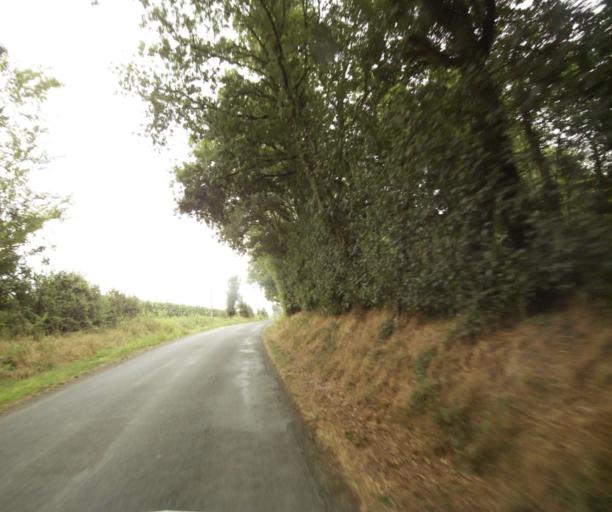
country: FR
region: Pays de la Loire
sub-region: Departement de la Sarthe
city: Juigne-sur-Sarthe
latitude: 47.8504
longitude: -0.2588
